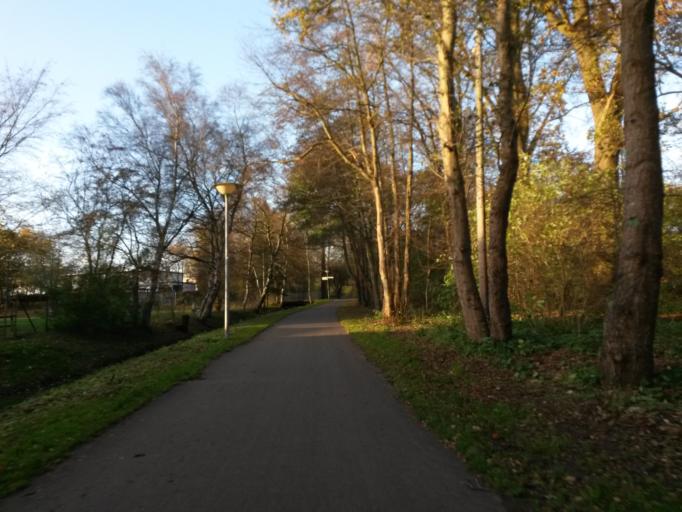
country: DE
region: Lower Saxony
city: Lilienthal
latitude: 53.0754
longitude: 8.9142
